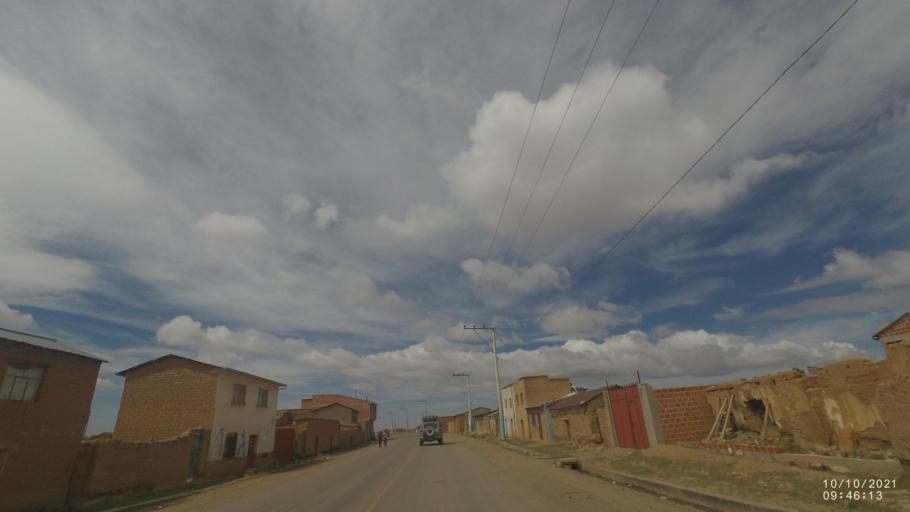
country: BO
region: La Paz
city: Quime
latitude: -17.1779
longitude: -67.3384
